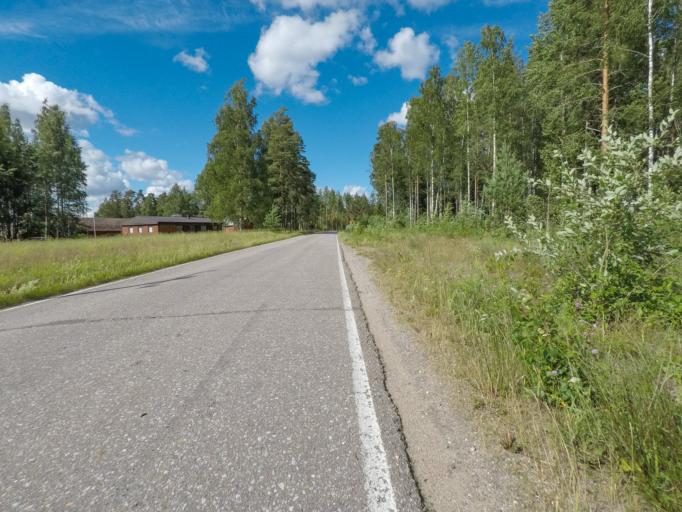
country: FI
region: South Karelia
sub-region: Lappeenranta
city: Joutseno
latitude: 61.1040
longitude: 28.3712
